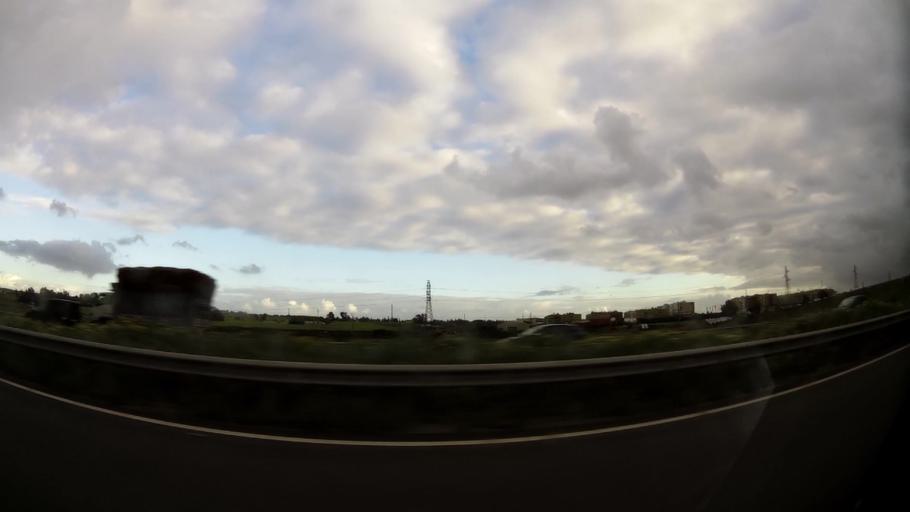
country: MA
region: Grand Casablanca
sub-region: Mediouna
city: Tit Mellil
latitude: 33.5657
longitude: -7.4828
